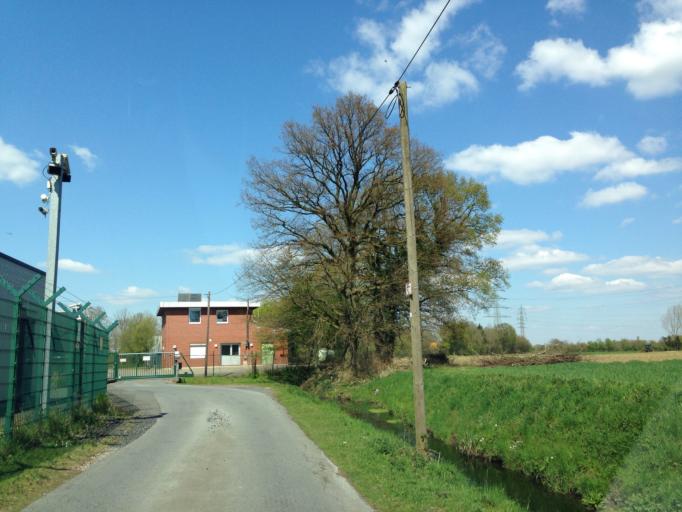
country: DE
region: North Rhine-Westphalia
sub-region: Regierungsbezirk Munster
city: Muenster
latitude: 51.9182
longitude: 7.5909
